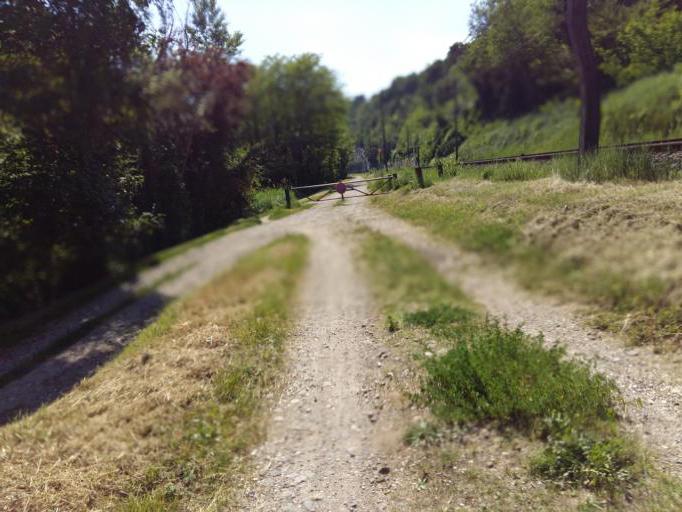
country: FR
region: Rhone-Alpes
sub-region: Departement du Rhone
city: Rillieux-la-Pape
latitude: 45.8036
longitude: 4.8919
